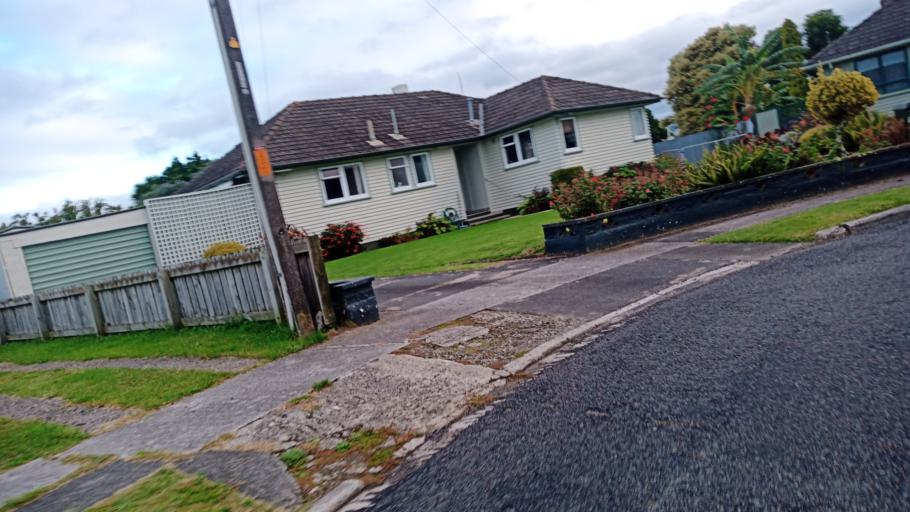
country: NZ
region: Gisborne
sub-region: Gisborne District
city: Gisborne
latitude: -38.6574
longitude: 177.9925
